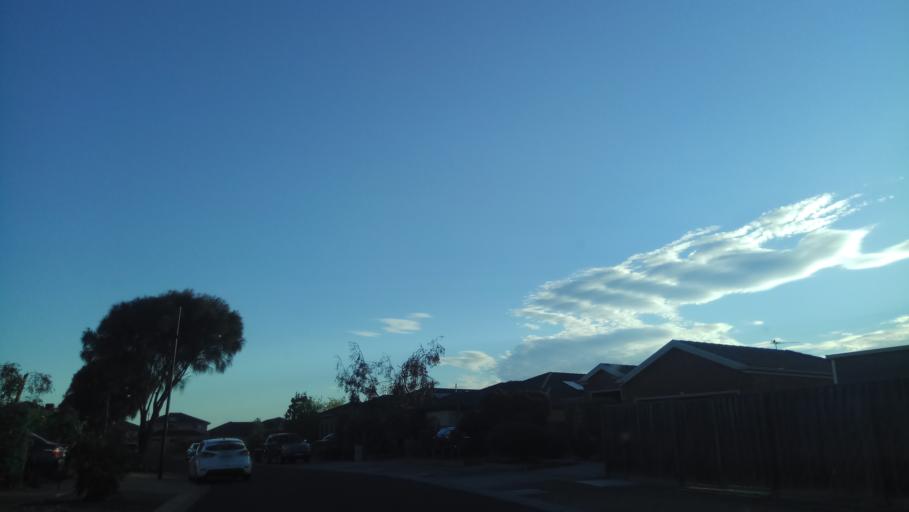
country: AU
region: Victoria
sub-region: Wyndham
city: Point Cook
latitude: -37.9071
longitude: 144.7487
